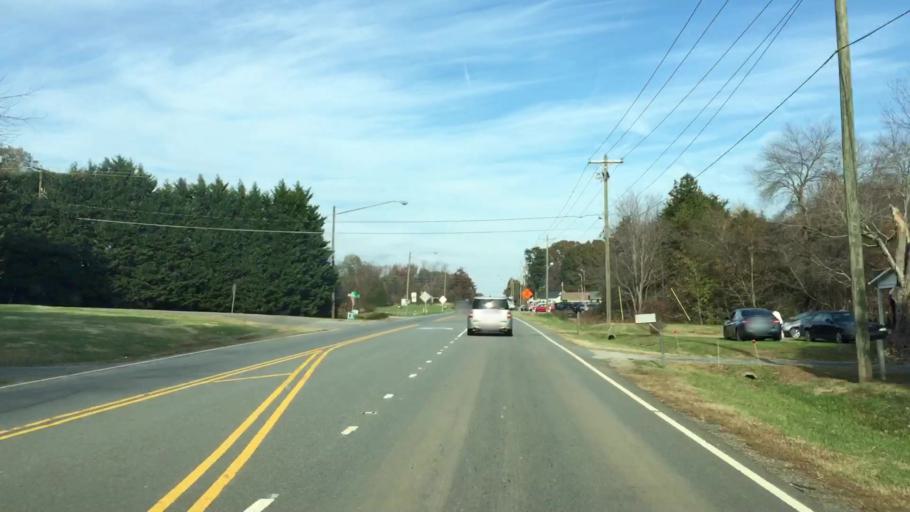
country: US
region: North Carolina
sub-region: Forsyth County
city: Walkertown
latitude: 36.1524
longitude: -80.1500
